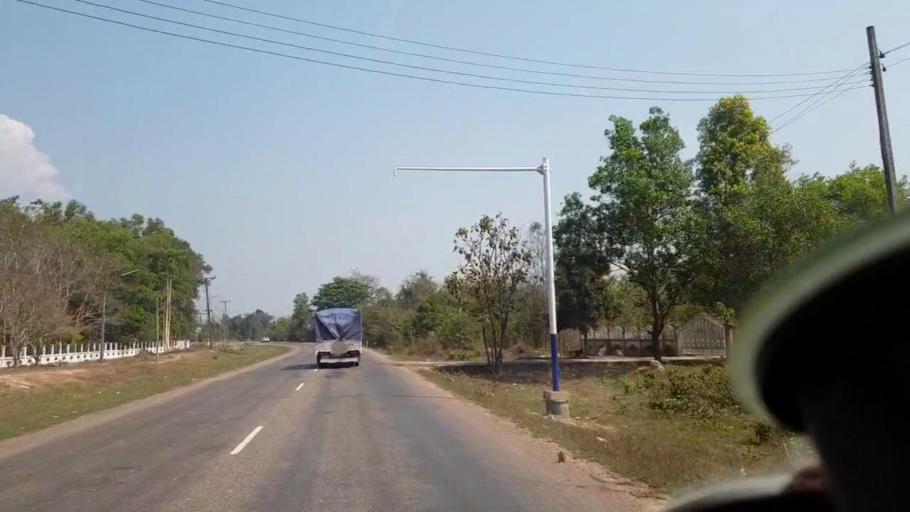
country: TH
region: Nong Khai
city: Phon Phisai
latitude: 18.1530
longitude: 103.0568
